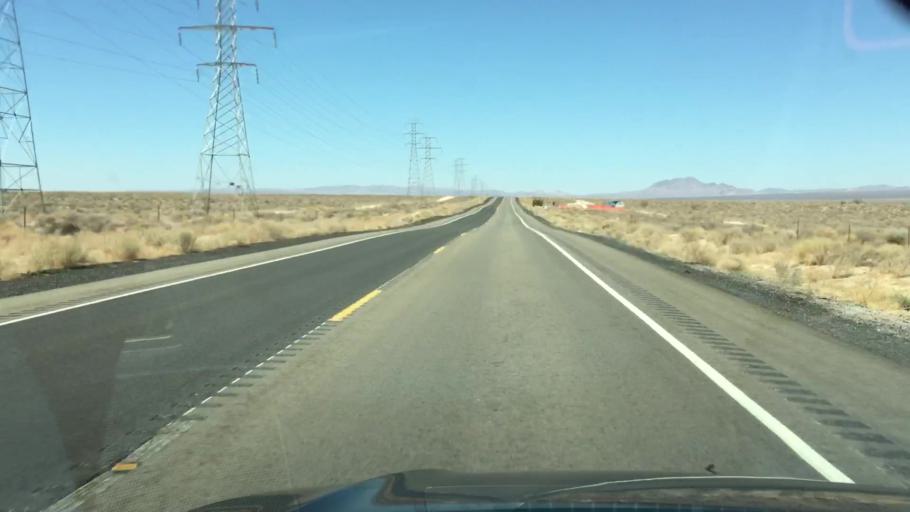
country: US
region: California
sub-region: Kern County
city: Boron
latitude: 35.1016
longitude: -117.5720
